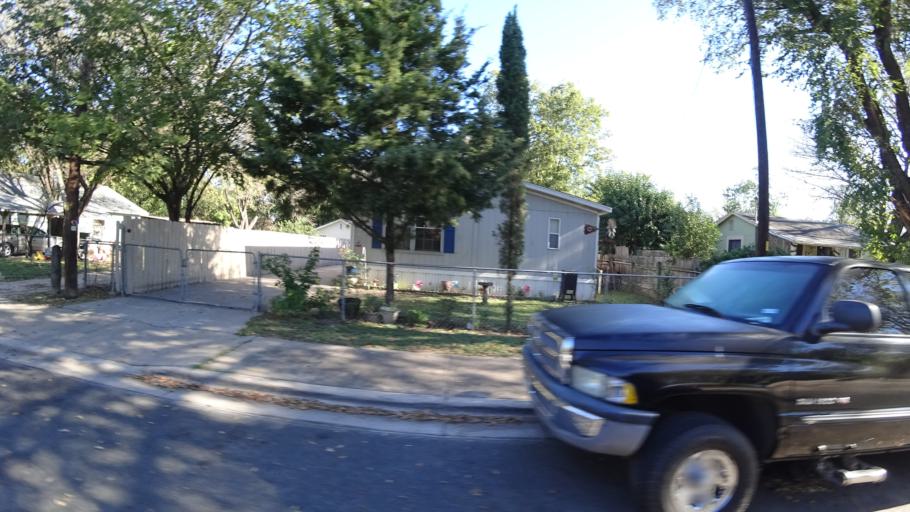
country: US
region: Texas
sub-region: Travis County
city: Austin
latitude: 30.2393
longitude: -97.6988
